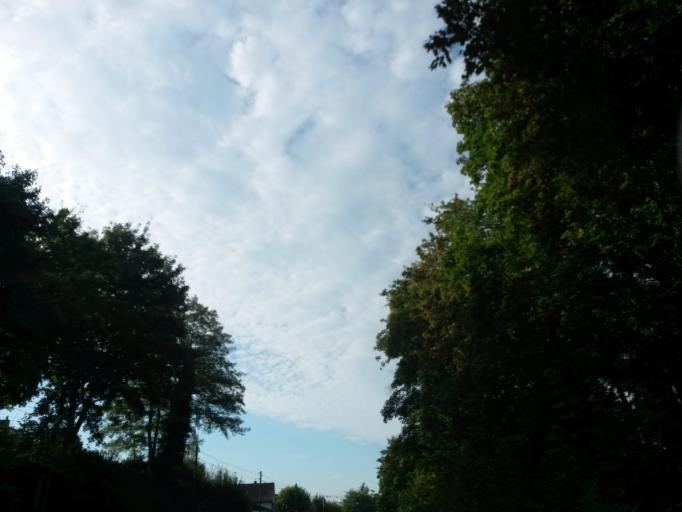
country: DE
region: North Rhine-Westphalia
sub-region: Regierungsbezirk Koln
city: Rosrath
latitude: 50.8839
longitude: 7.1908
